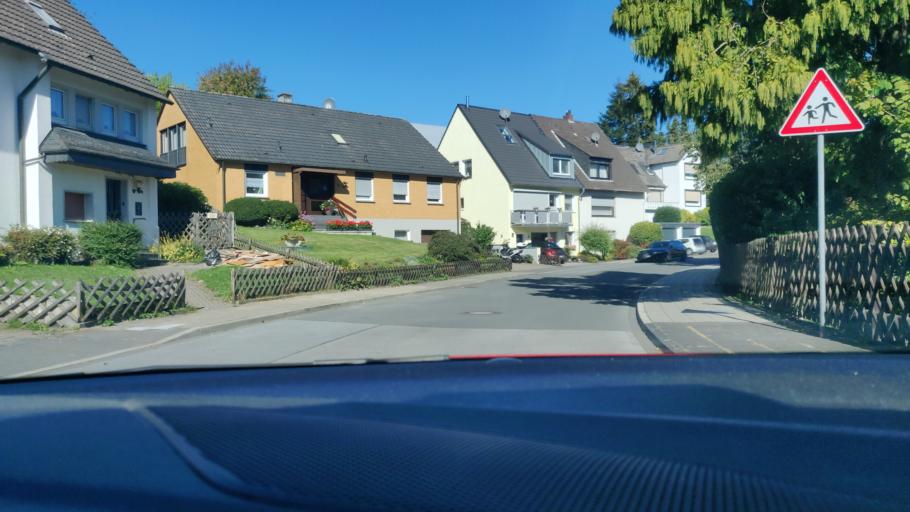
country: DE
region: North Rhine-Westphalia
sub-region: Regierungsbezirk Dusseldorf
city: Velbert
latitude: 51.3400
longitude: 7.0668
